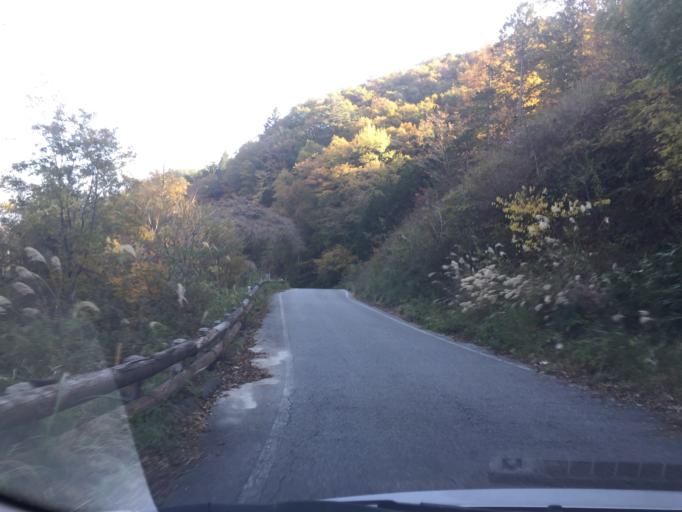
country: JP
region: Nagano
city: Iida
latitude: 35.3730
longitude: 137.6927
